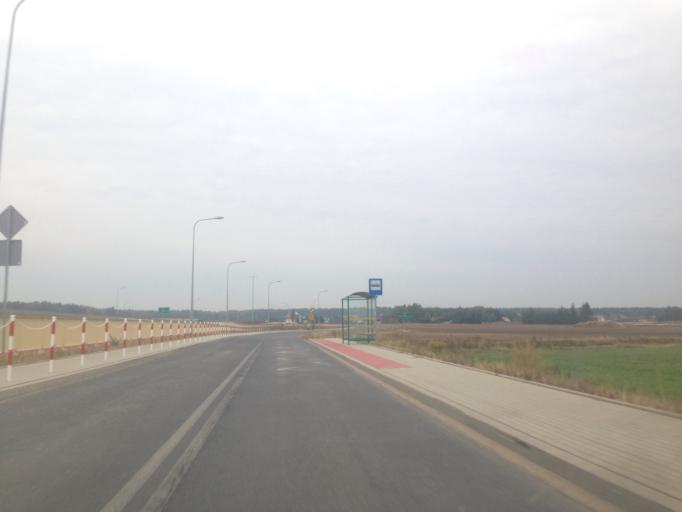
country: PL
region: Greater Poland Voivodeship
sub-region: Powiat gnieznienski
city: Lubowo
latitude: 52.4581
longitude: 17.3859
